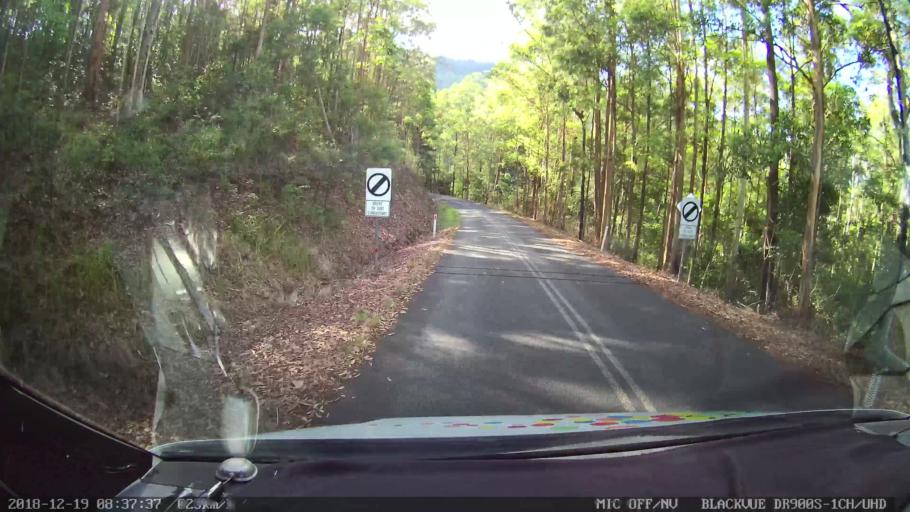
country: AU
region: New South Wales
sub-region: Kyogle
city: Kyogle
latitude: -28.3321
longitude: 152.9732
